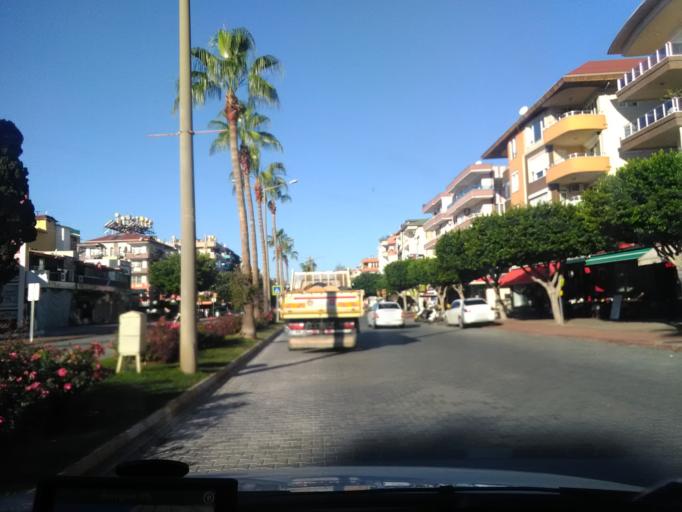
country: TR
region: Antalya
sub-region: Alanya
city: Alanya
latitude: 36.5463
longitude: 31.9896
